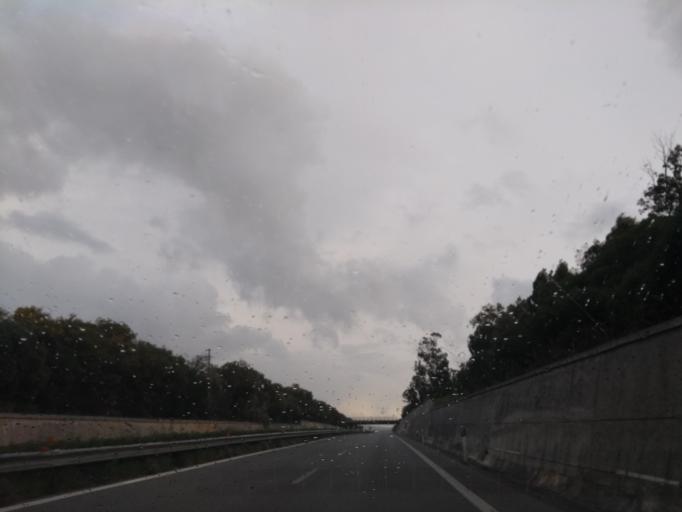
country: IT
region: Sicily
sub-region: Trapani
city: Paceco
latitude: 37.9715
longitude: 12.6110
